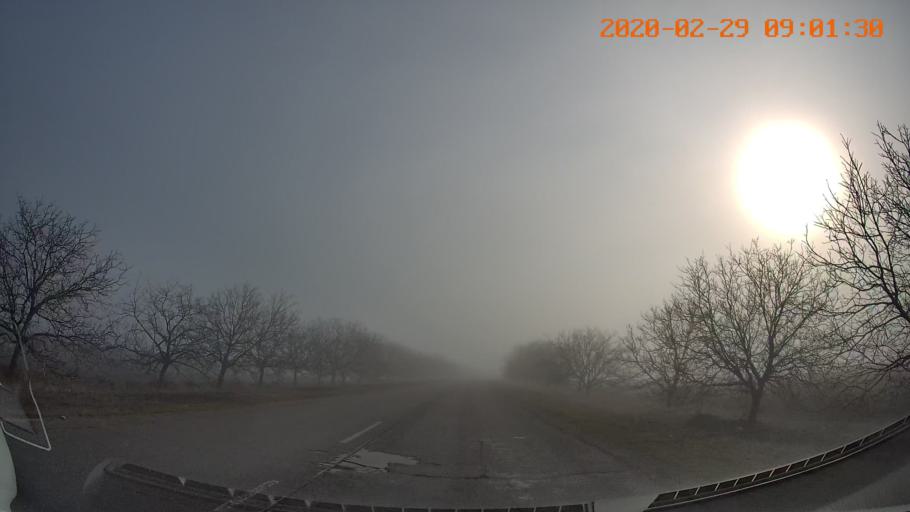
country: UA
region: Odessa
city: Velykoploske
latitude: 46.9238
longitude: 29.6935
